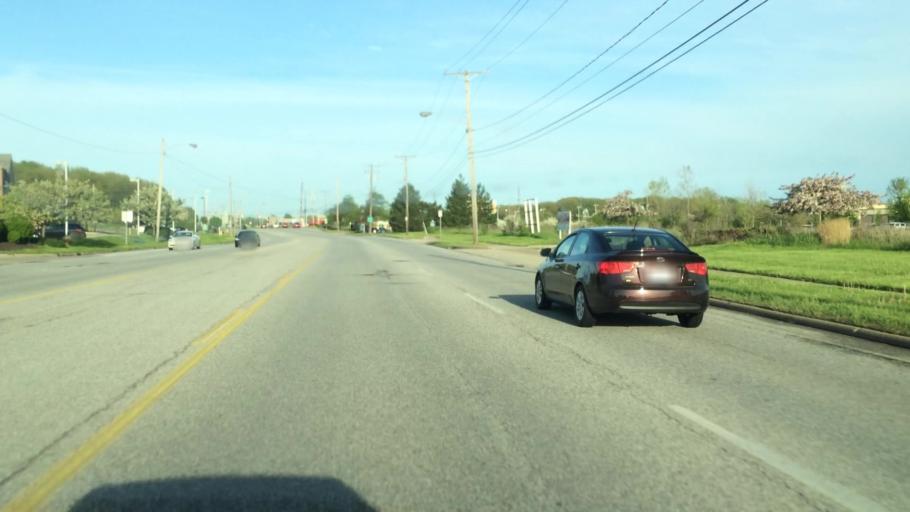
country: US
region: Ohio
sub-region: Cuyahoga County
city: Bedford Heights
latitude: 41.4091
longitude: -81.5312
